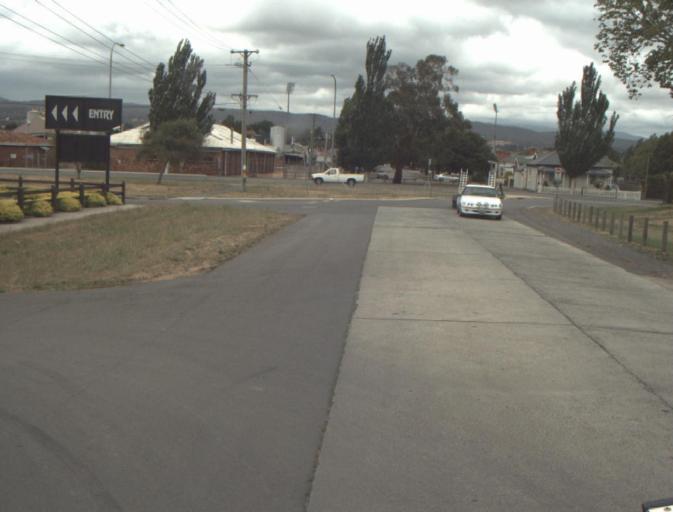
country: AU
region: Tasmania
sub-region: Launceston
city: Launceston
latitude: -41.4277
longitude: 147.1309
